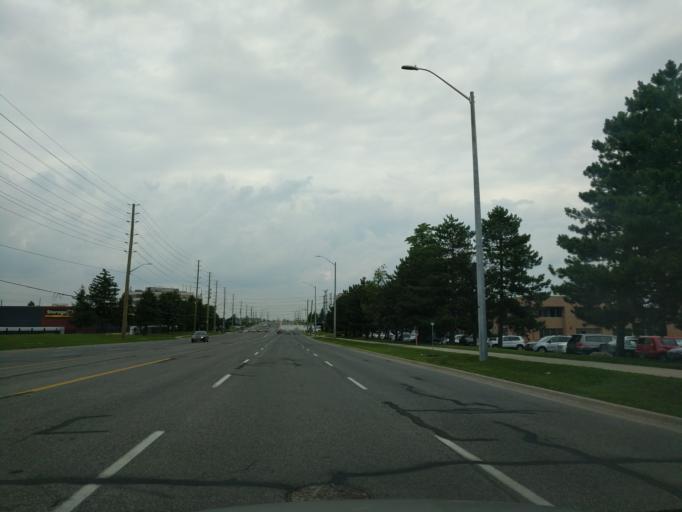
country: CA
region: Ontario
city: Markham
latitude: 43.8352
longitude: -79.3285
